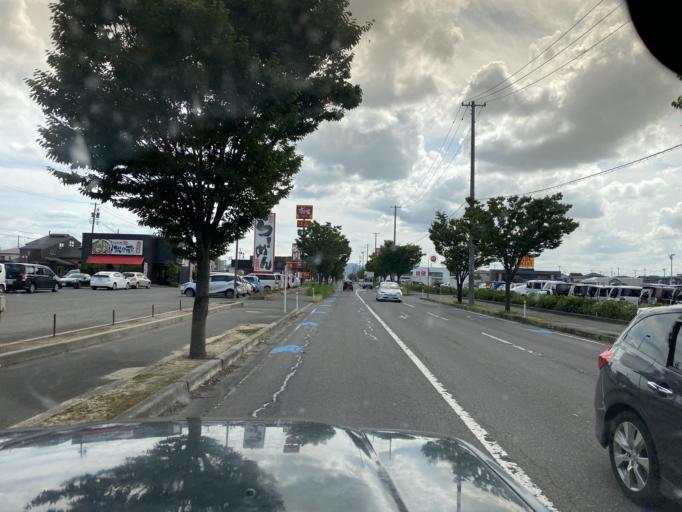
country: JP
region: Niigata
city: Niitsu-honcho
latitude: 37.8062
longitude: 139.1151
